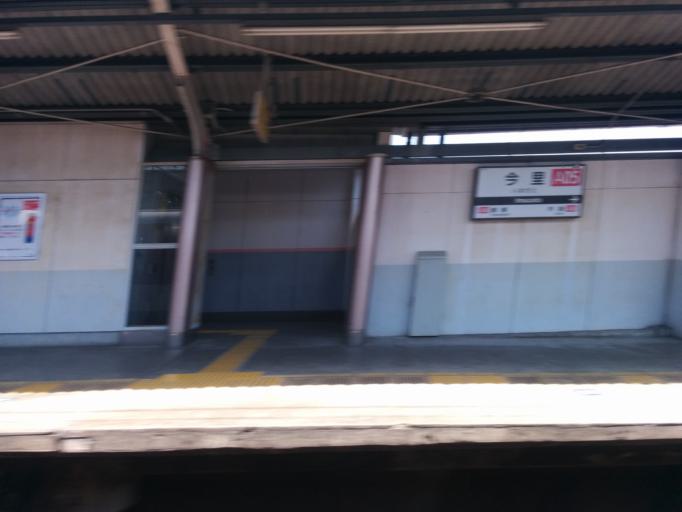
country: JP
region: Osaka
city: Osaka-shi
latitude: 34.6648
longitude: 135.5496
